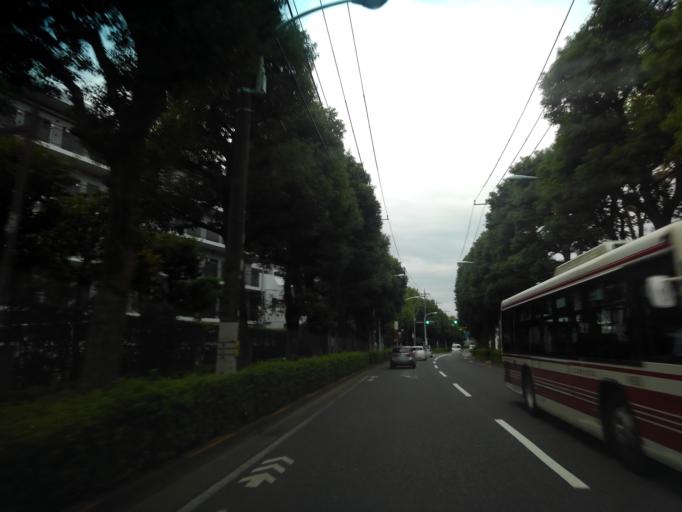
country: JP
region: Tokyo
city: Chofugaoka
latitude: 35.6596
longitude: 139.5407
